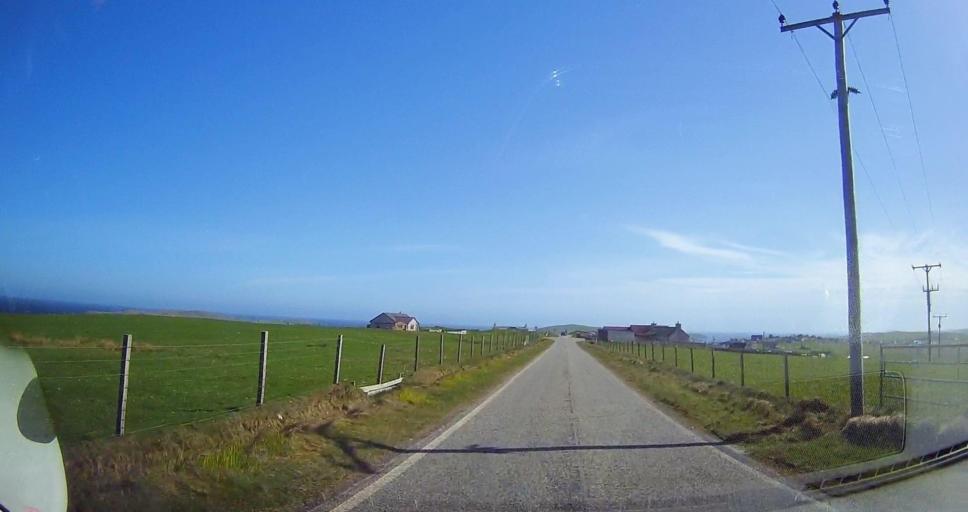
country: GB
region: Scotland
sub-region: Shetland Islands
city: Sandwick
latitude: 60.0162
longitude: -1.2292
